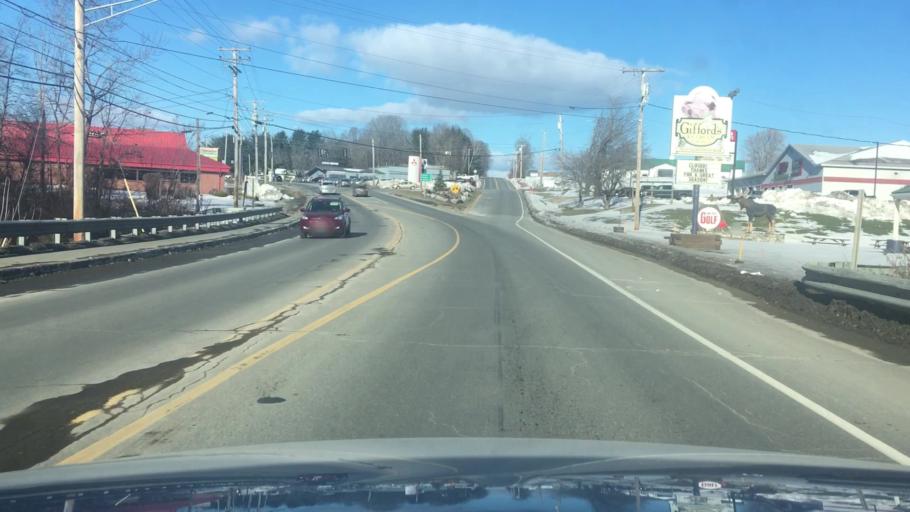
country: US
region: Maine
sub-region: Somerset County
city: Skowhegan
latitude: 44.7824
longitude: -69.7273
